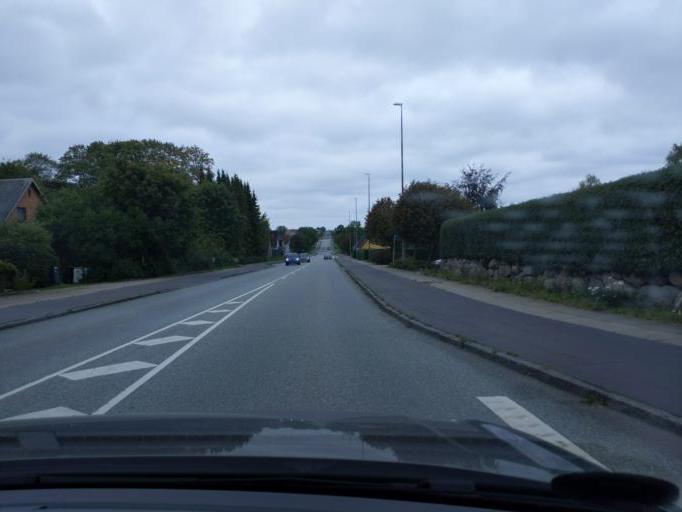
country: DK
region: Central Jutland
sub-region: Randers Kommune
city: Spentrup
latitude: 56.5137
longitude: 9.9483
